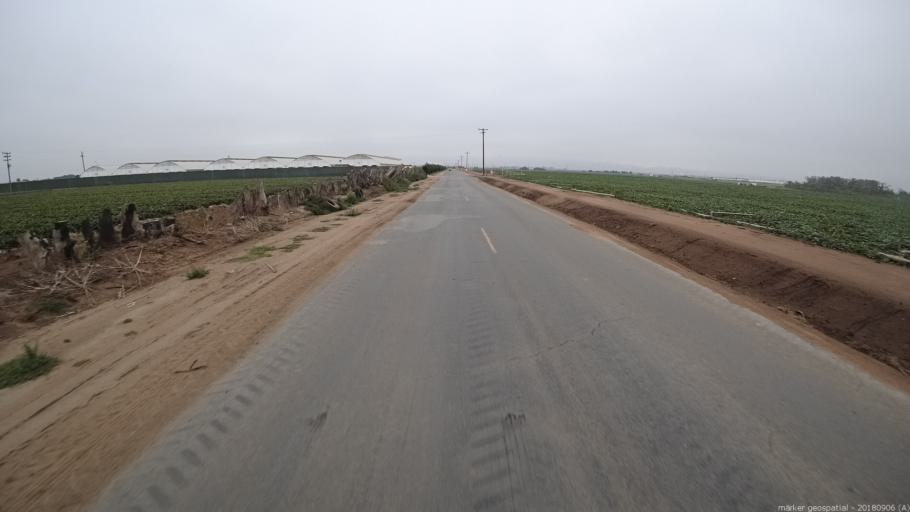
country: US
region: California
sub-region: Monterey County
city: Chualar
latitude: 36.6473
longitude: -121.5652
